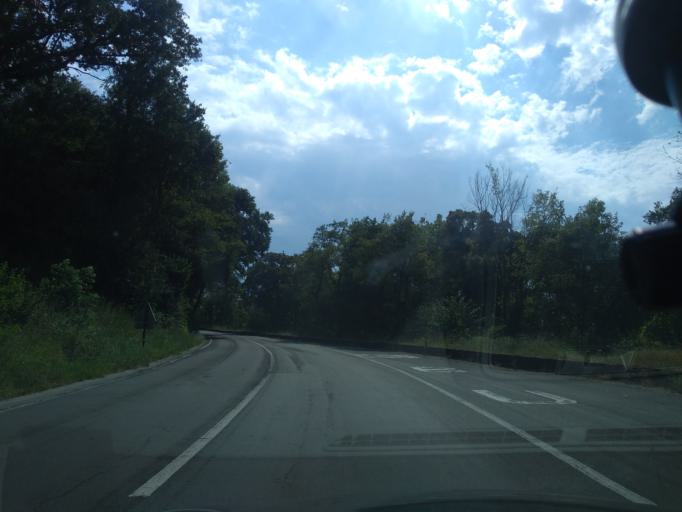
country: BE
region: Wallonia
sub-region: Province de Namur
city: Dinant
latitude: 50.2328
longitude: 4.8912
